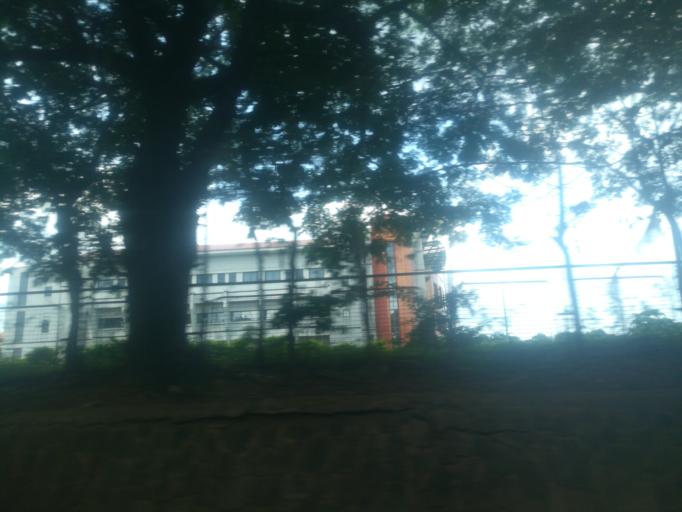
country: NG
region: Oyo
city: Ibadan
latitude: 7.4456
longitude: 3.8941
